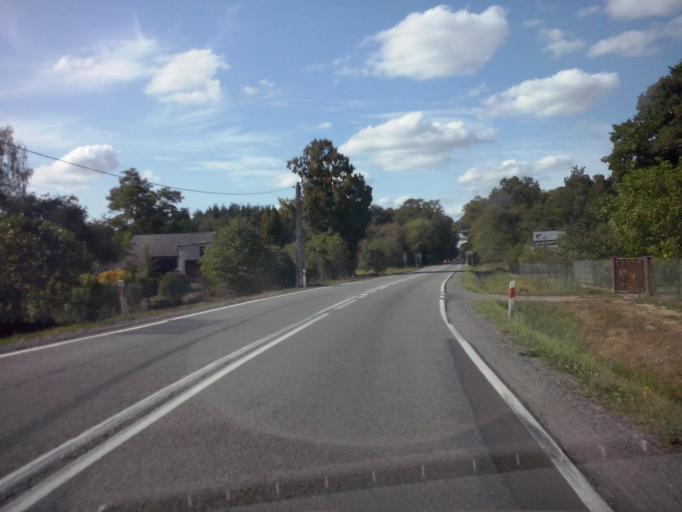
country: PL
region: Subcarpathian Voivodeship
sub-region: Powiat nizanski
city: Raclawice
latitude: 50.5025
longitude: 22.1784
